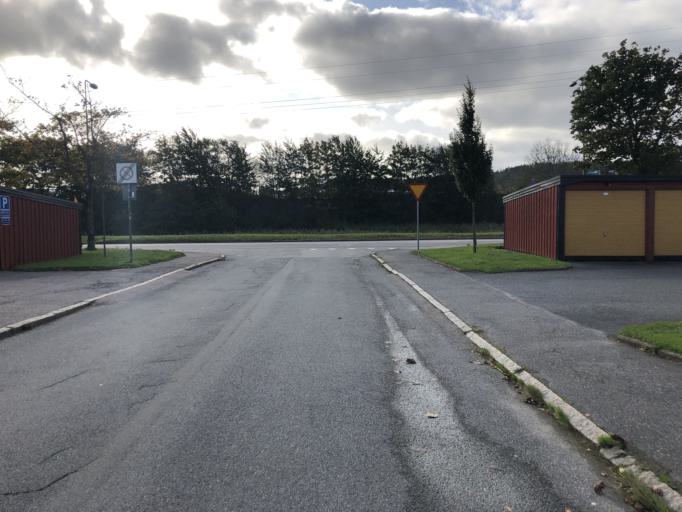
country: SE
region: Vaestra Goetaland
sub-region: Molndal
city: Moelndal
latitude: 57.6452
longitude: 12.0101
